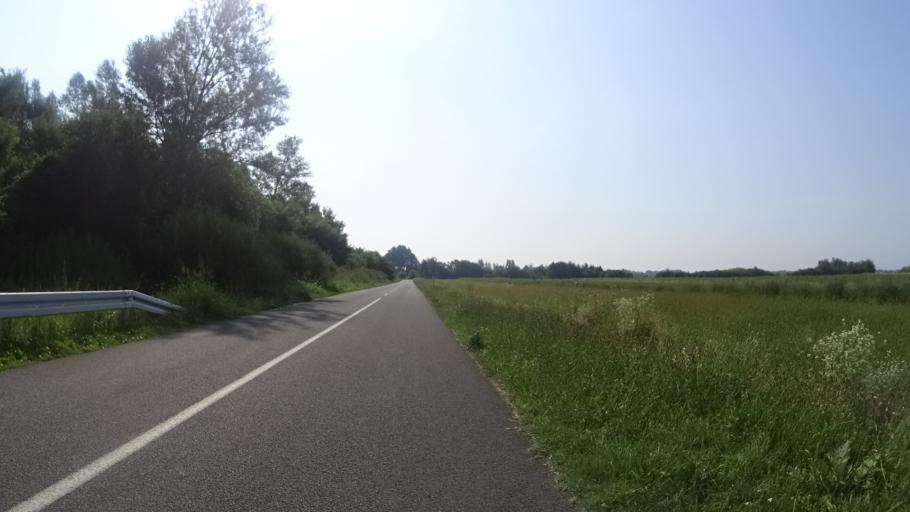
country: HR
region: Medimurska
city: Belica
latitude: 46.3945
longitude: 16.5295
